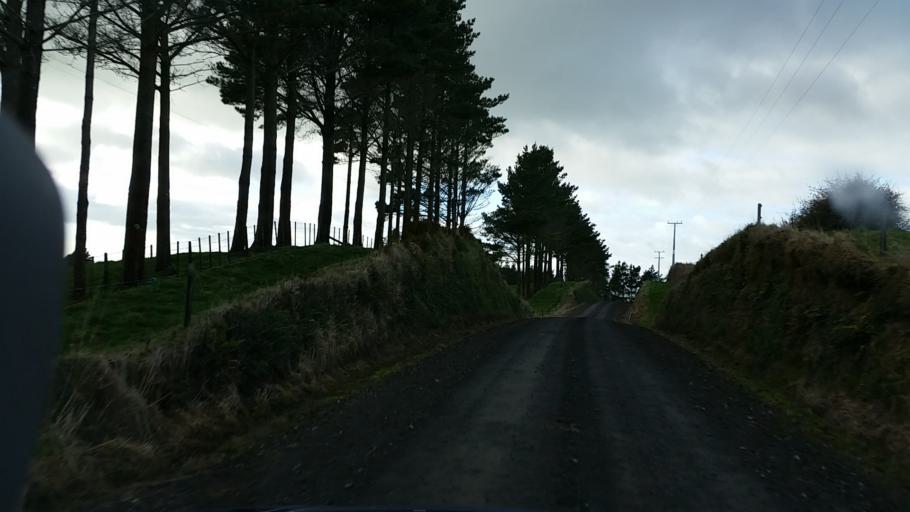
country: NZ
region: Taranaki
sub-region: South Taranaki District
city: Eltham
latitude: -39.3370
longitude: 174.1835
